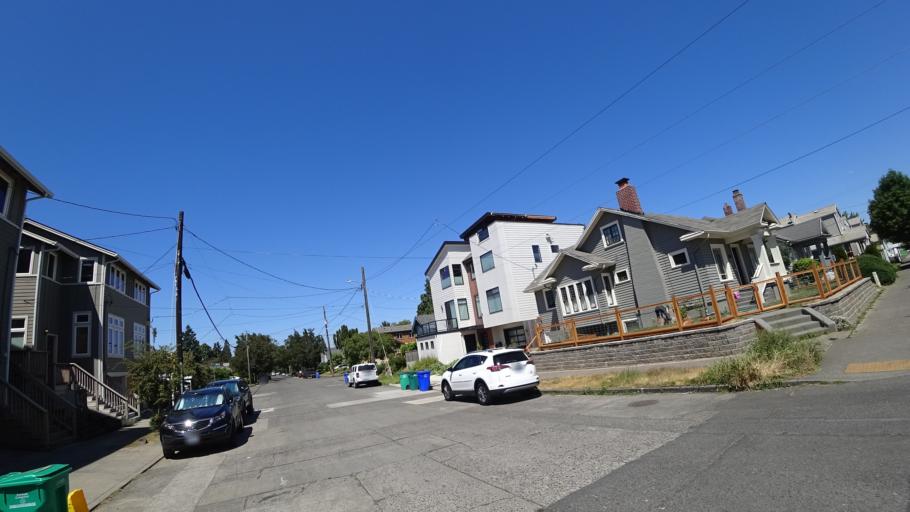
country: US
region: Oregon
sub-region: Multnomah County
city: Portland
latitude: 45.5628
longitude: -122.6521
